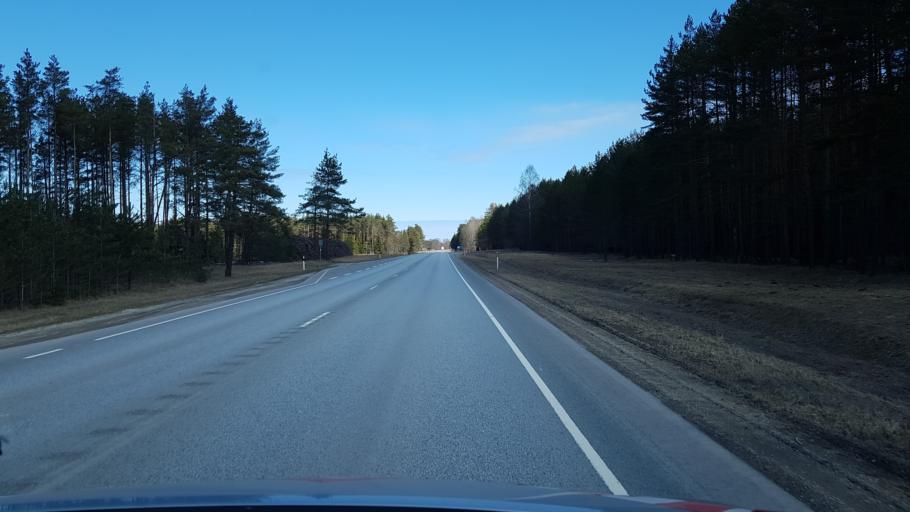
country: EE
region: Laeaene-Virumaa
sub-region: Viru-Nigula vald
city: Kunda
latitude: 59.3972
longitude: 26.6268
